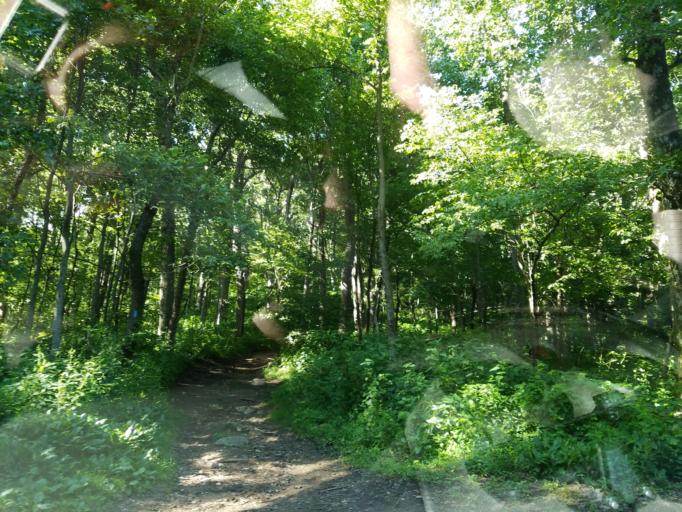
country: US
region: Georgia
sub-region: Dawson County
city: Dawsonville
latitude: 34.6086
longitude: -84.2144
